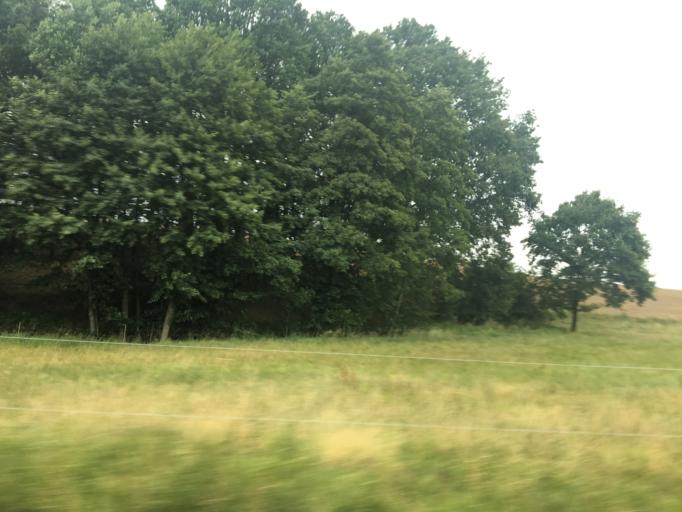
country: DE
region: Saxony
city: Wilsdruff
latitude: 51.0665
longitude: 13.5894
